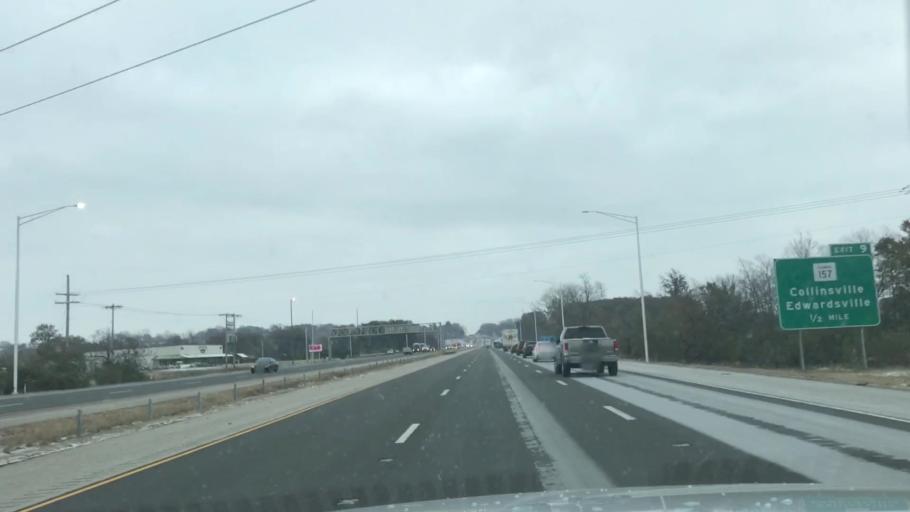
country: US
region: Illinois
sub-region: Madison County
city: Glen Carbon
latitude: 38.7568
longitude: -90.0250
